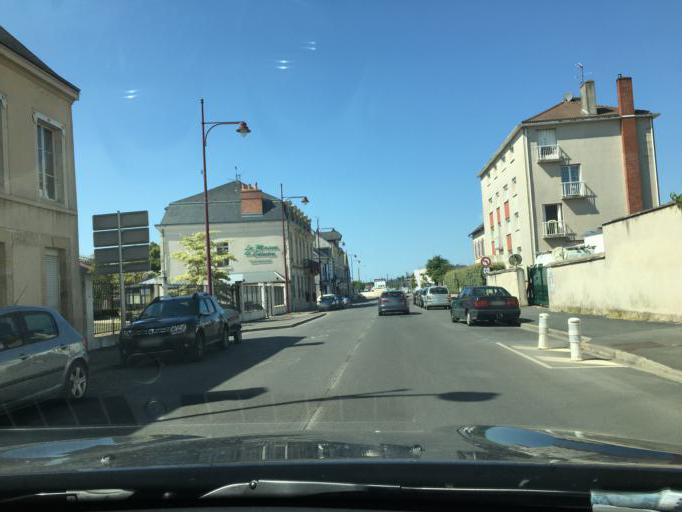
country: FR
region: Centre
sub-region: Departement du Cher
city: Vierzon
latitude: 47.2253
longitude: 2.0612
